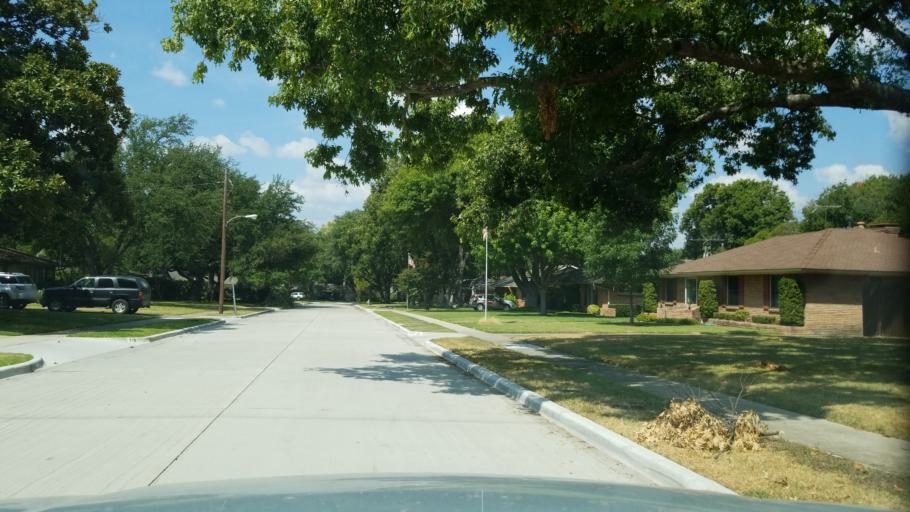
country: US
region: Texas
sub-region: Dallas County
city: Richardson
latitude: 32.9558
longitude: -96.7458
